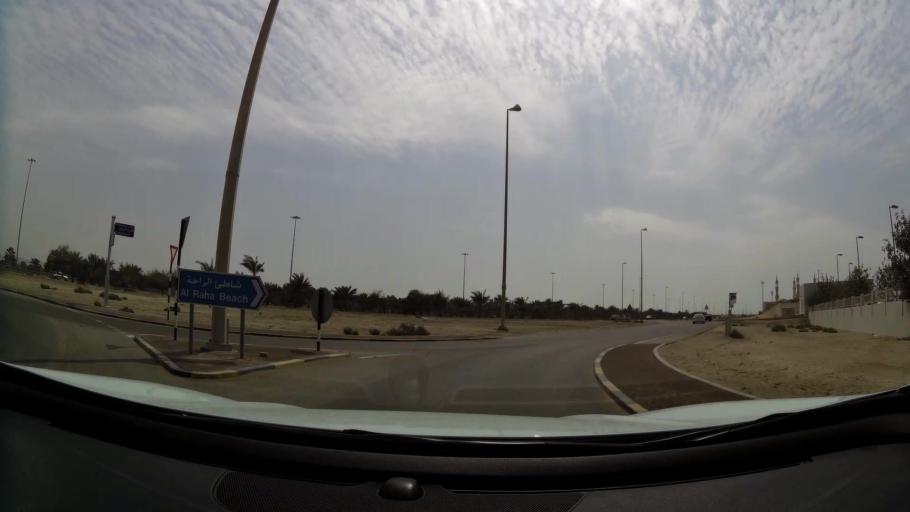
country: AE
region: Abu Dhabi
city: Abu Dhabi
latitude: 24.5203
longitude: 54.6695
